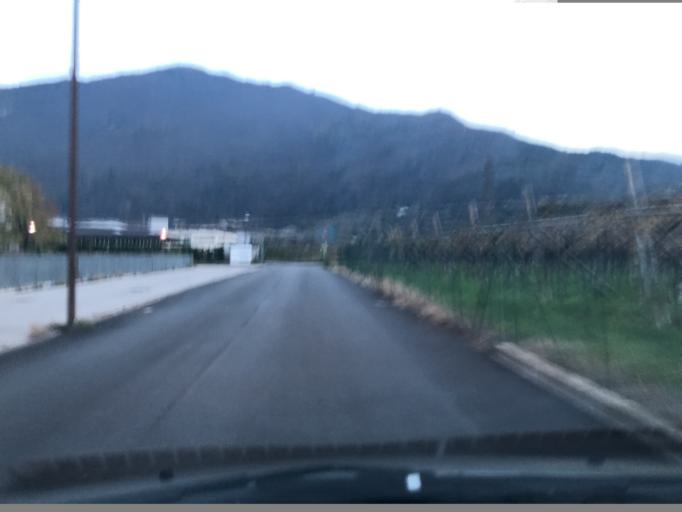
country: IT
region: Trentino-Alto Adige
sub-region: Provincia di Trento
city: Arco
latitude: 45.8986
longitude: 10.8758
